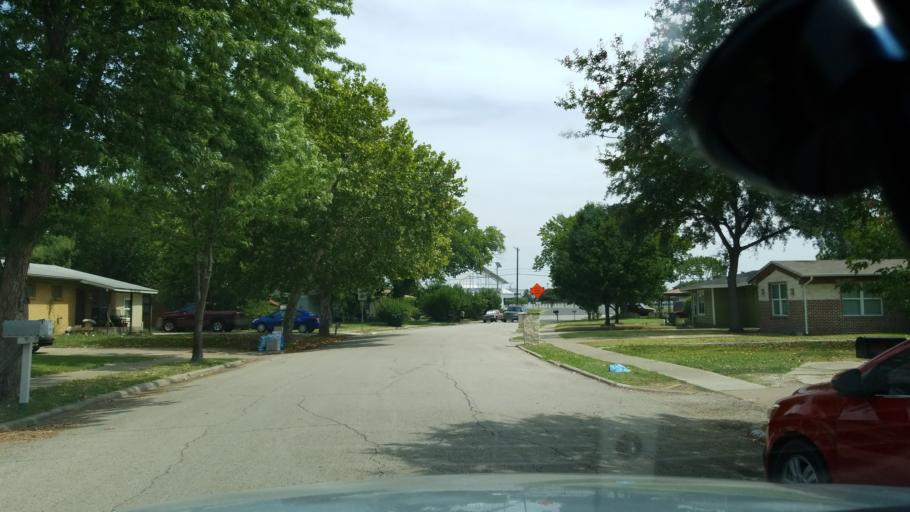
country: US
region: Texas
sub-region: Dallas County
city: Irving
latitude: 32.8318
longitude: -96.9879
